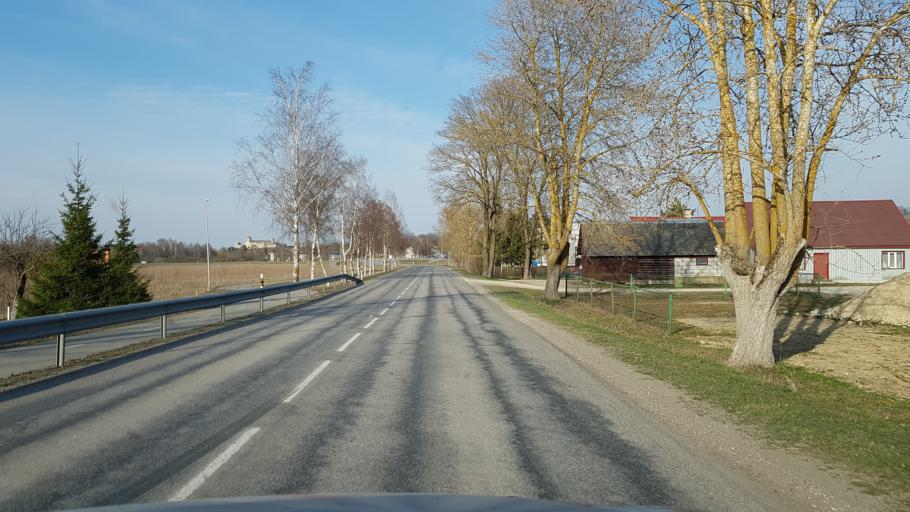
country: EE
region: Laeaene-Virumaa
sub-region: Rakvere linn
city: Rakvere
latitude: 59.3378
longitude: 26.3384
